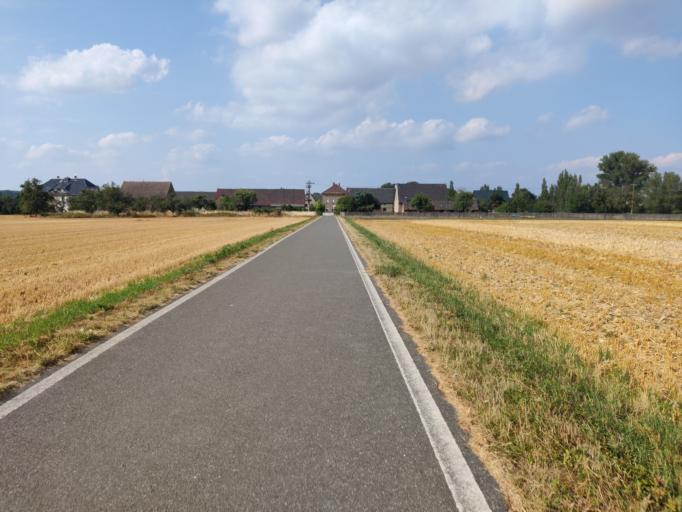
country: DE
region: Thuringia
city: Fockendorf
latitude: 51.0419
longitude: 12.4584
